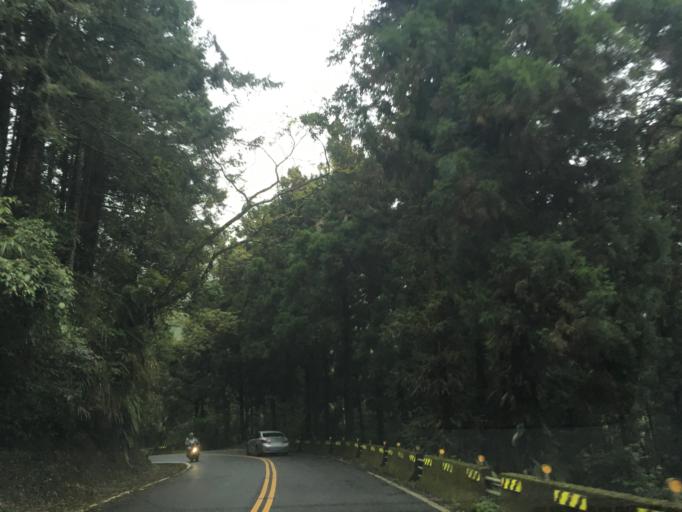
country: TW
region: Taiwan
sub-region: Chiayi
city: Jiayi Shi
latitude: 23.4990
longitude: 120.7005
